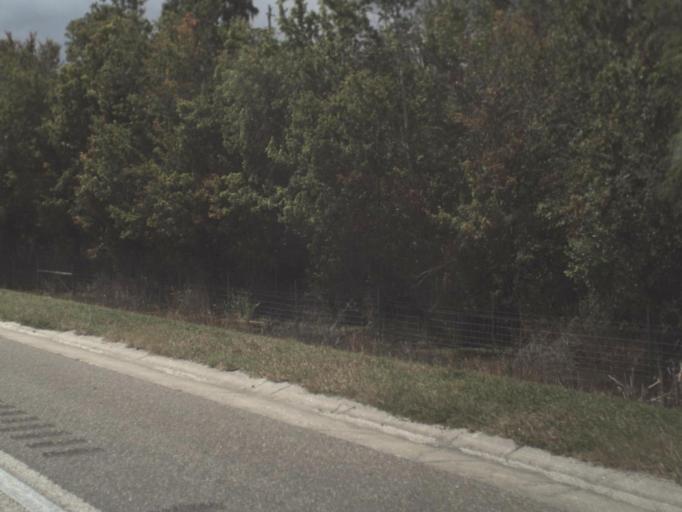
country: US
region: Florida
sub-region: Polk County
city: Lake Alfred
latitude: 28.1980
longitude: -81.7066
